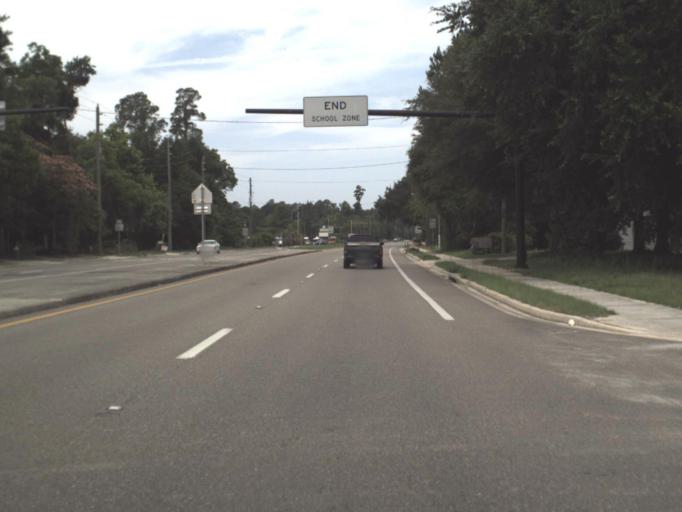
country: US
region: Florida
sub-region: Alachua County
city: Hawthorne
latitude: 29.5963
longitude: -82.0929
